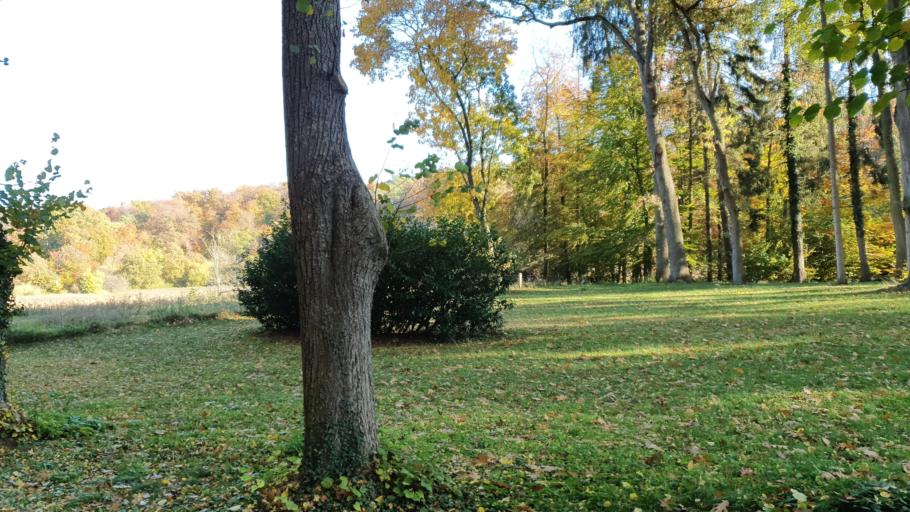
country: DE
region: Mecklenburg-Vorpommern
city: Crivitz
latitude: 53.6386
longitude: 11.6281
